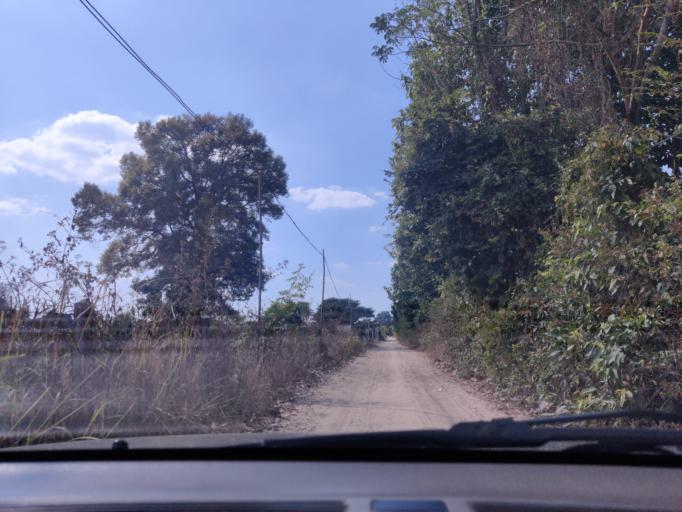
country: TH
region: Sisaket
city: Si Sa Ket
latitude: 15.1000
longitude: 104.3613
